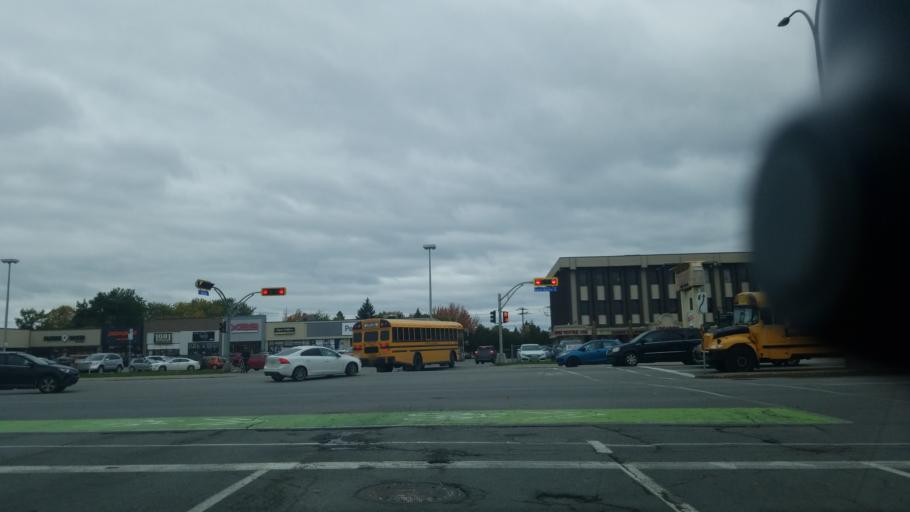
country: CA
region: Quebec
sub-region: Laval
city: Laval
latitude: 45.5672
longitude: -73.7286
